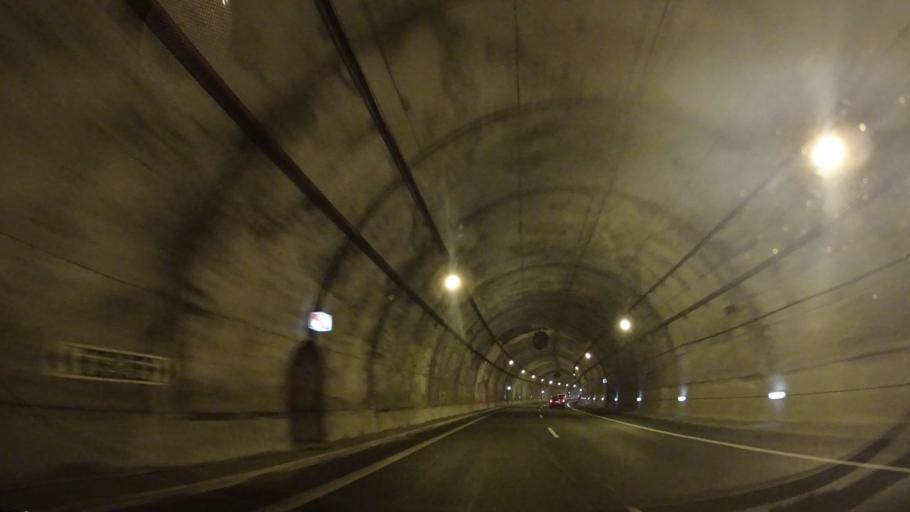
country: ES
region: Asturias
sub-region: Province of Asturias
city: Arriba
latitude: 43.5055
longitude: -5.5817
